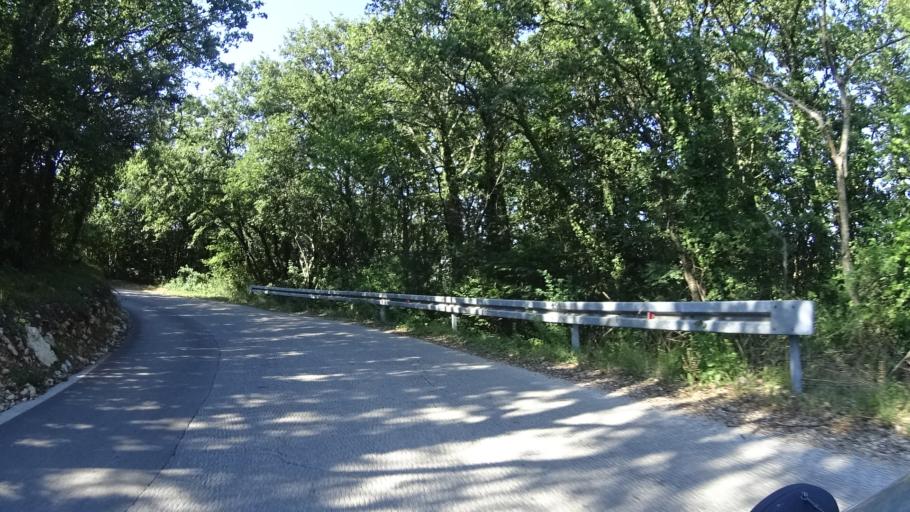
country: HR
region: Istarska
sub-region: Grad Labin
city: Labin
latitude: 45.0711
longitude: 14.1214
